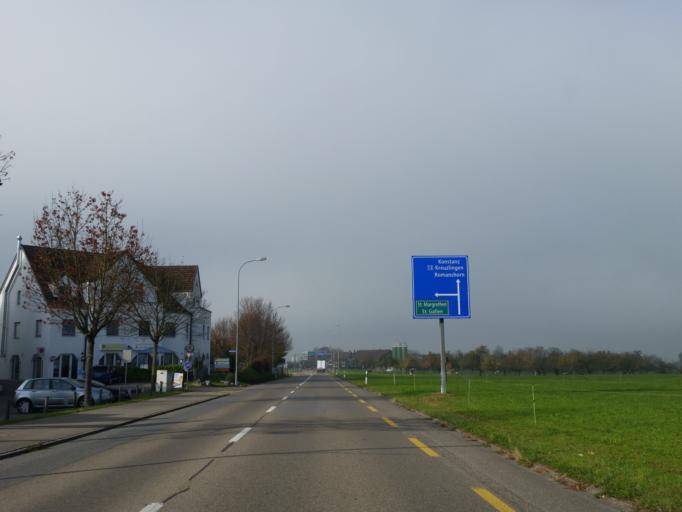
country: CH
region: Thurgau
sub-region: Arbon District
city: Egnach
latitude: 47.5304
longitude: 9.4025
